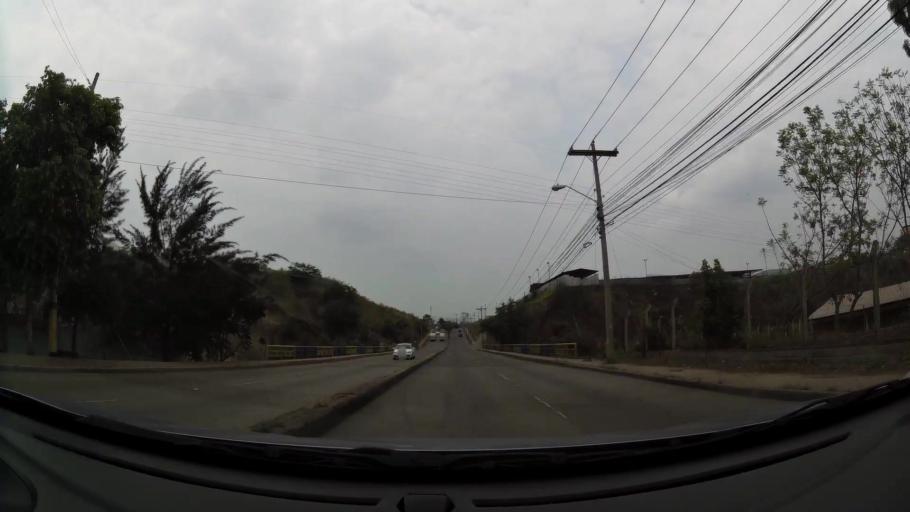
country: HN
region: Francisco Morazan
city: Tegucigalpa
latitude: 14.0686
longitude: -87.1995
